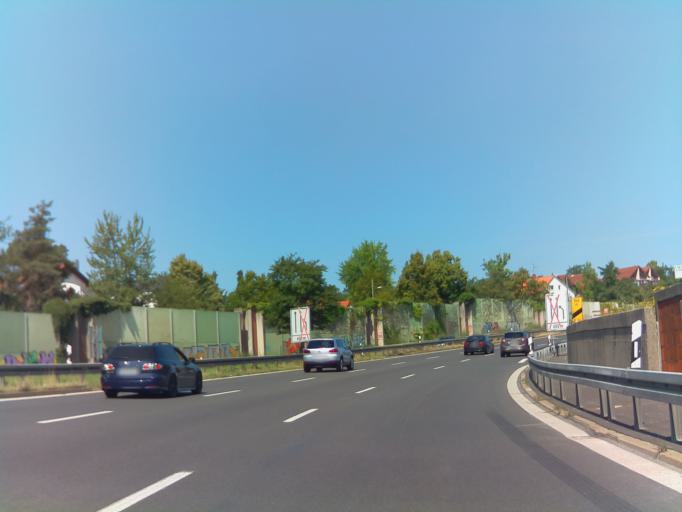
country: DE
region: Baden-Wuerttemberg
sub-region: Regierungsbezirk Stuttgart
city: Gerlingen
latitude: 48.7428
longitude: 9.1106
